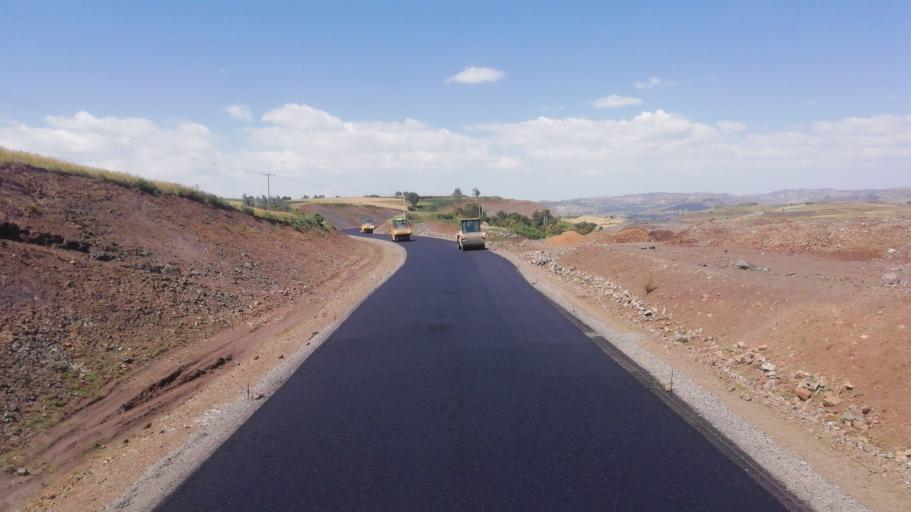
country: ET
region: Amhara
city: Addiet Canna
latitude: 11.3633
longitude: 37.8712
